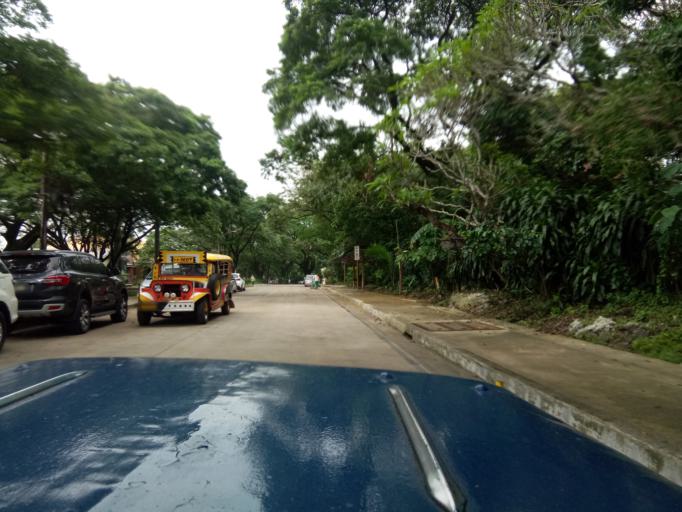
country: PH
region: Metro Manila
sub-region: Quezon City
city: Quezon City
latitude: 14.6511
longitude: 121.0659
